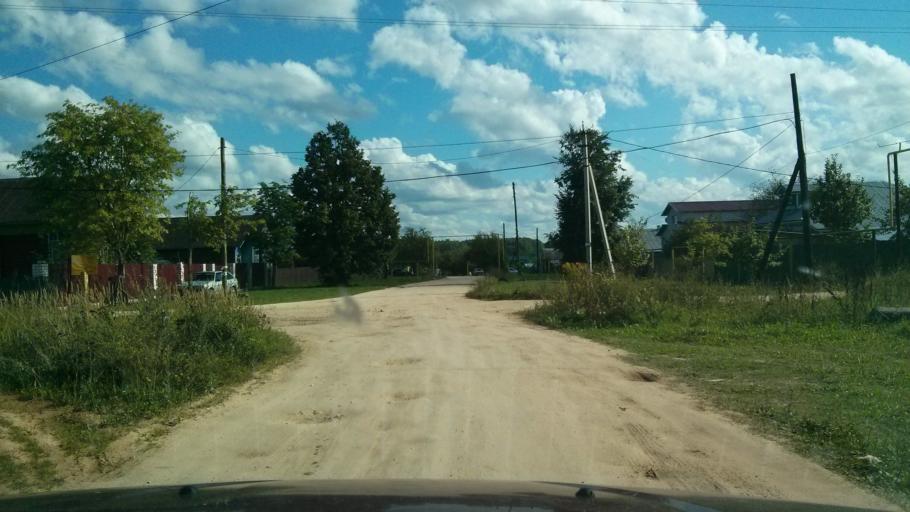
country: RU
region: Nizjnij Novgorod
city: Vacha
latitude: 55.7596
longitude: 42.5159
